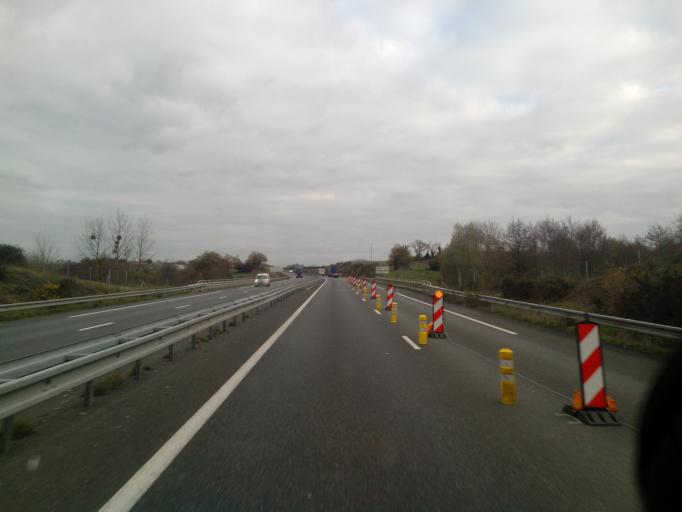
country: FR
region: Poitou-Charentes
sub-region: Departement des Deux-Sevres
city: Le Pin
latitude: 46.8984
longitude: -0.6525
